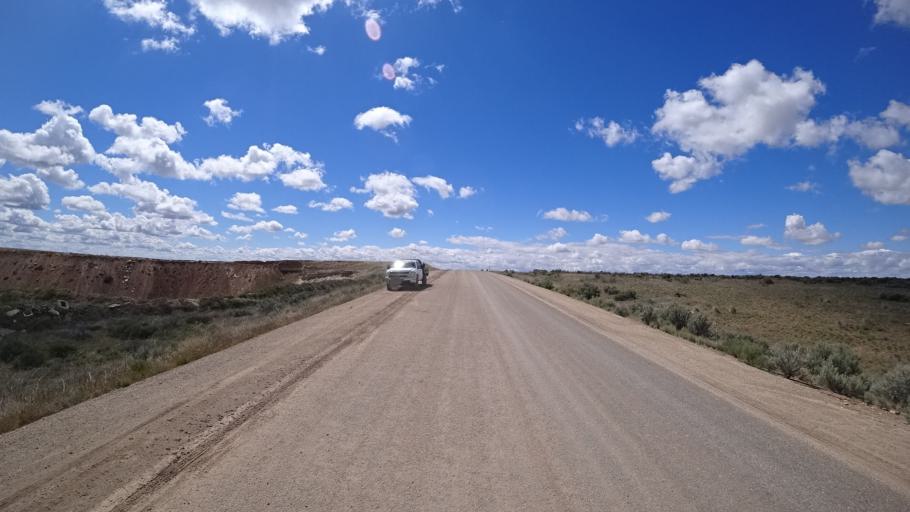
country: US
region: Idaho
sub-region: Ada County
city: Garden City
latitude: 43.4861
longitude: -116.2743
